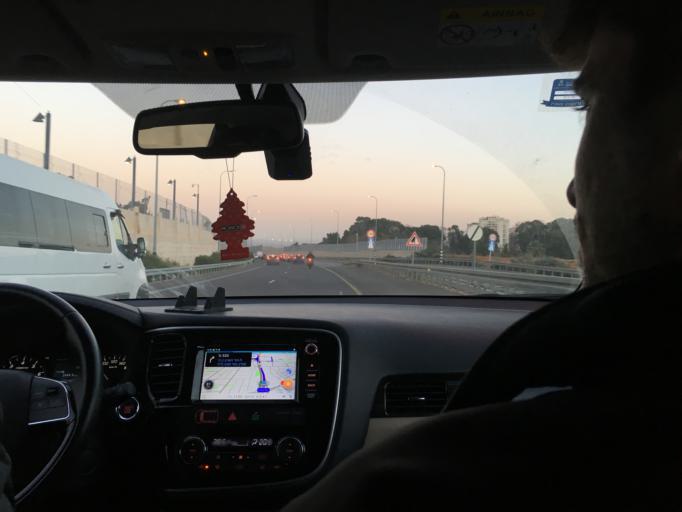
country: IL
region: Central District
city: Kfar Saba
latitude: 32.1696
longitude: 34.9025
